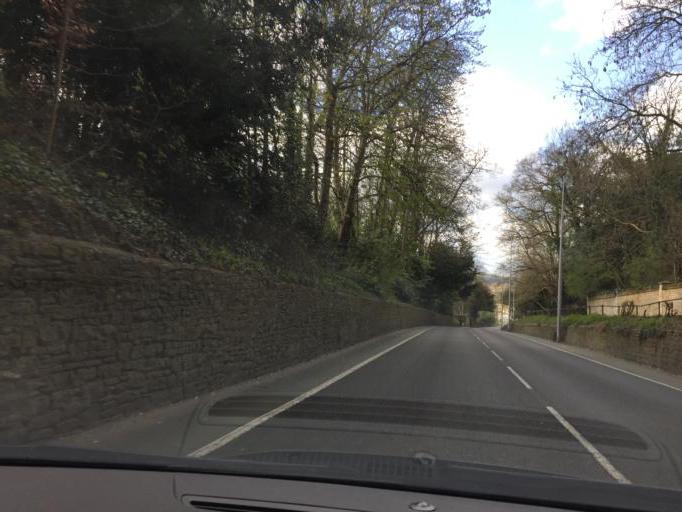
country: GB
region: England
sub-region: Oxfordshire
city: Oxford
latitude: 51.7541
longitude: -1.2306
